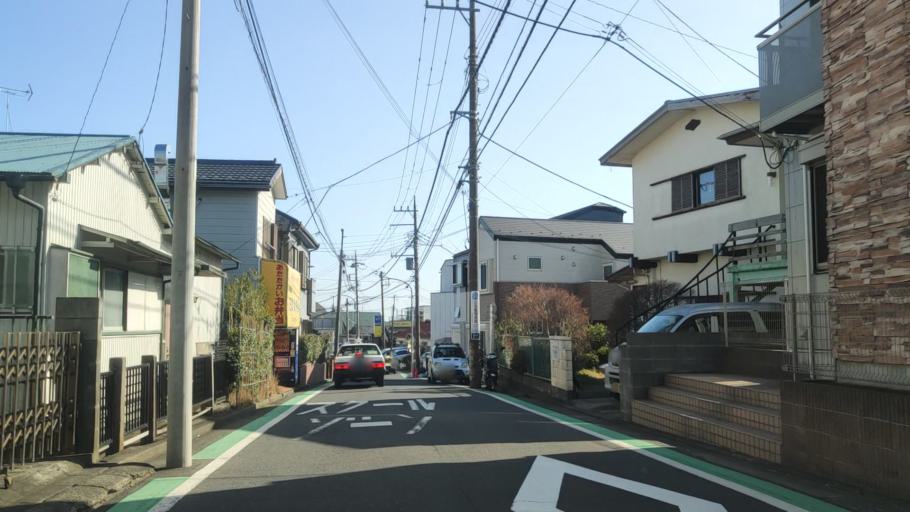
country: JP
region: Kanagawa
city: Yokohama
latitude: 35.4644
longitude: 139.5992
